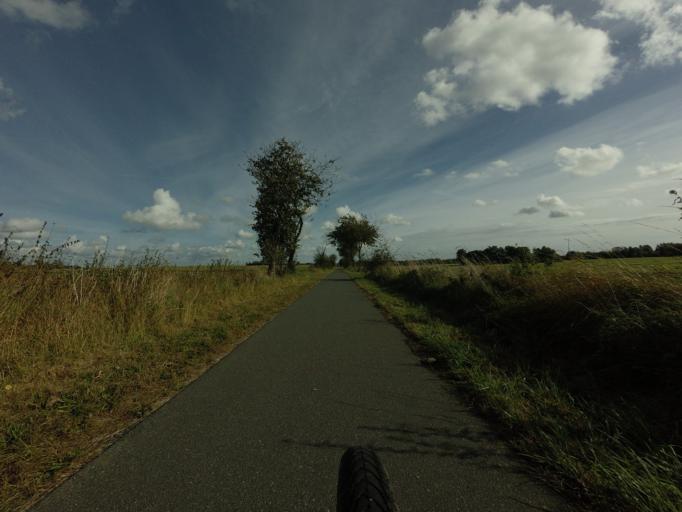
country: DK
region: Central Jutland
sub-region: Viborg Kommune
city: Bjerringbro
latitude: 56.4923
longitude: 9.6580
